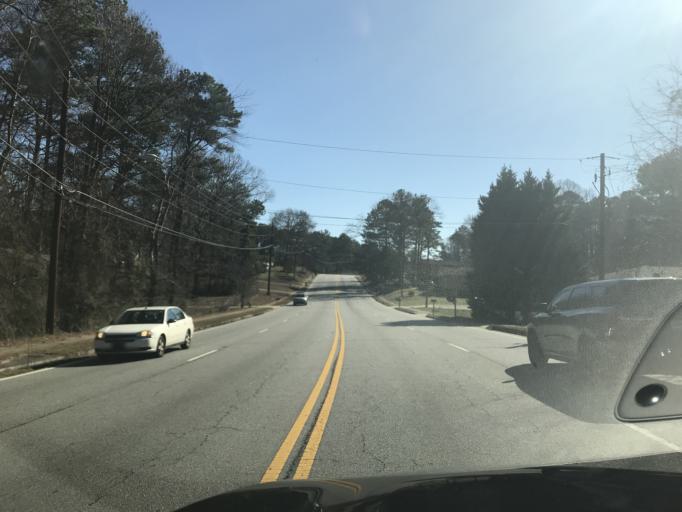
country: US
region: Georgia
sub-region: Cobb County
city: Mableton
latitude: 33.7858
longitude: -84.5754
